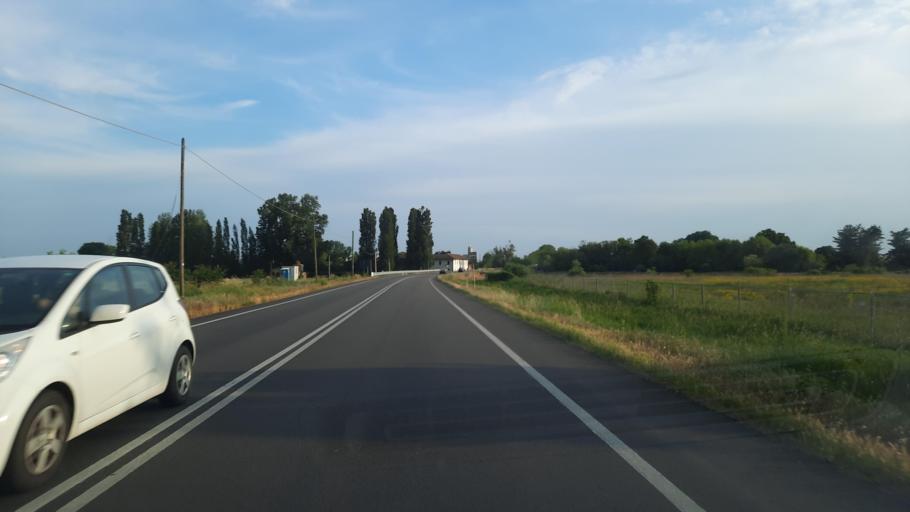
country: IT
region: Lombardy
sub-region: Provincia di Pavia
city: Mortara
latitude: 45.2491
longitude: 8.7532
